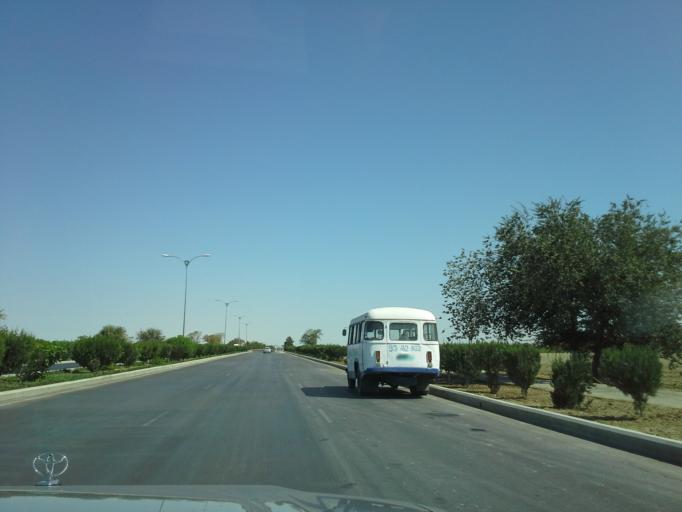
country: TM
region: Ahal
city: Annau
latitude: 37.9062
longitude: 58.5266
